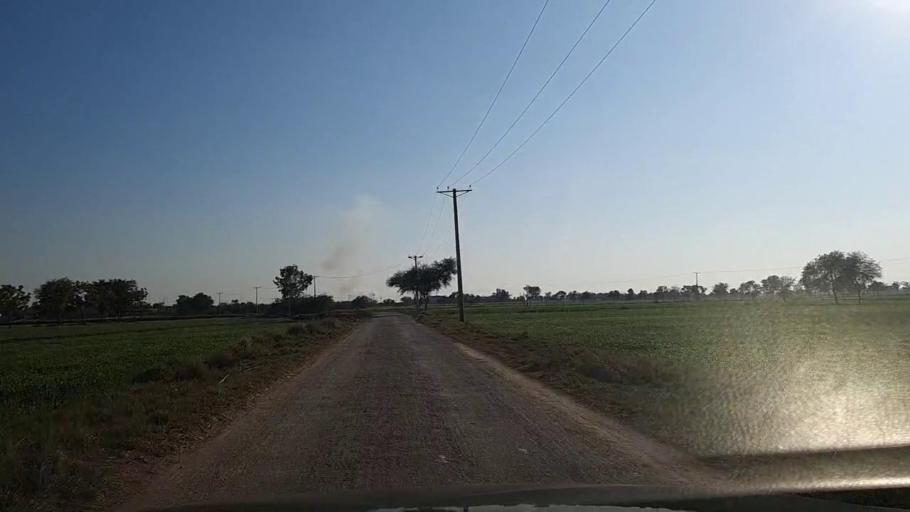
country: PK
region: Sindh
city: Nawabshah
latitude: 26.2078
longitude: 68.3750
